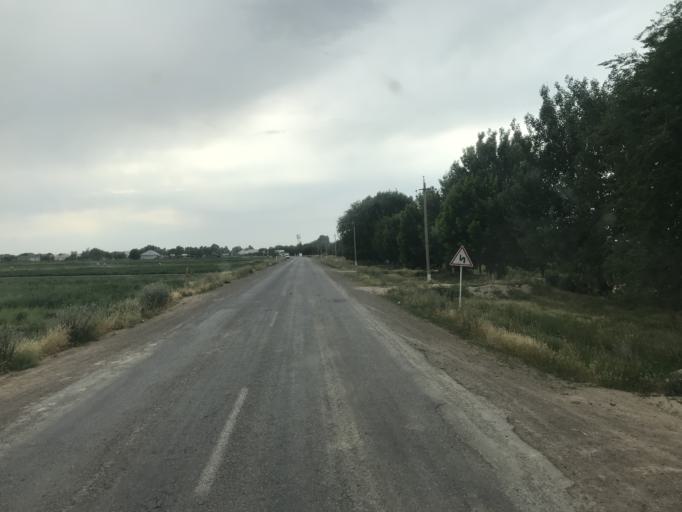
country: KZ
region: Ongtustik Qazaqstan
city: Asykata
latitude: 40.9531
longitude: 68.4346
